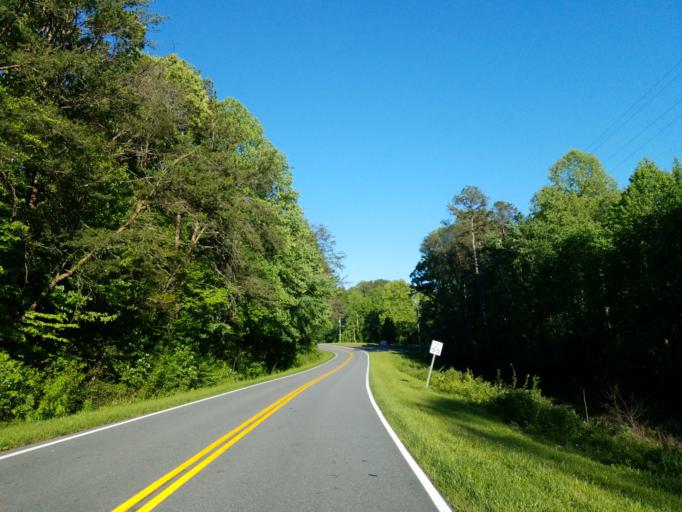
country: US
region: Georgia
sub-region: Gilmer County
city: Ellijay
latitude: 34.6790
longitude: -84.3295
